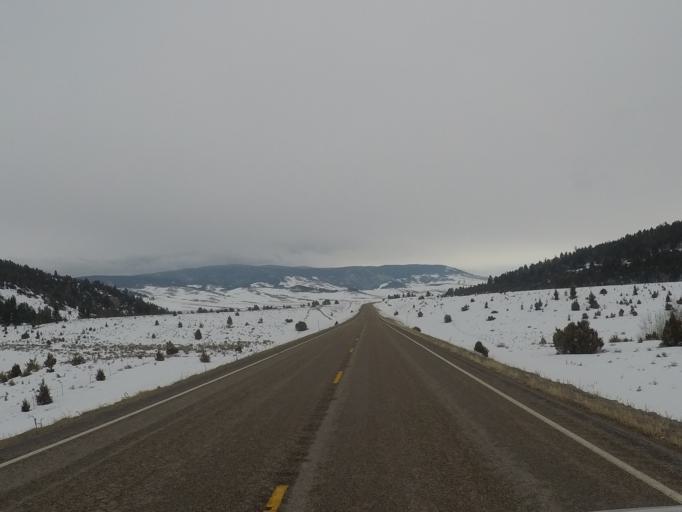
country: US
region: Montana
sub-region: Meagher County
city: White Sulphur Springs
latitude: 46.6135
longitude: -110.8438
